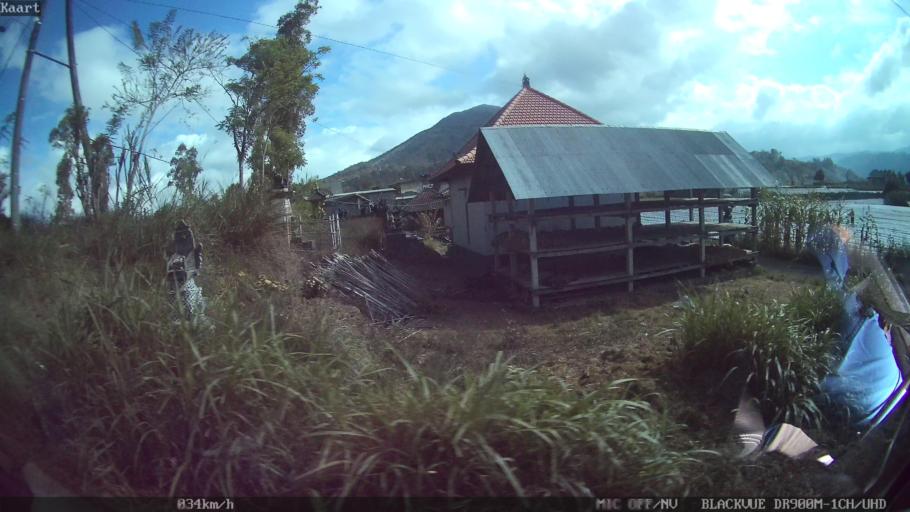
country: ID
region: Bali
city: Banjar Trunyan
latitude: -8.2198
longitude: 115.3923
